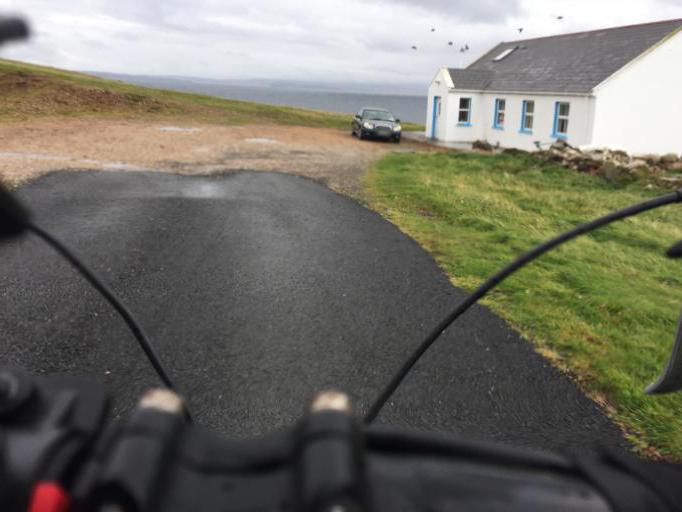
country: IE
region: Ulster
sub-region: County Donegal
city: Derrybeg
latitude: 55.2556
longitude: -8.1959
